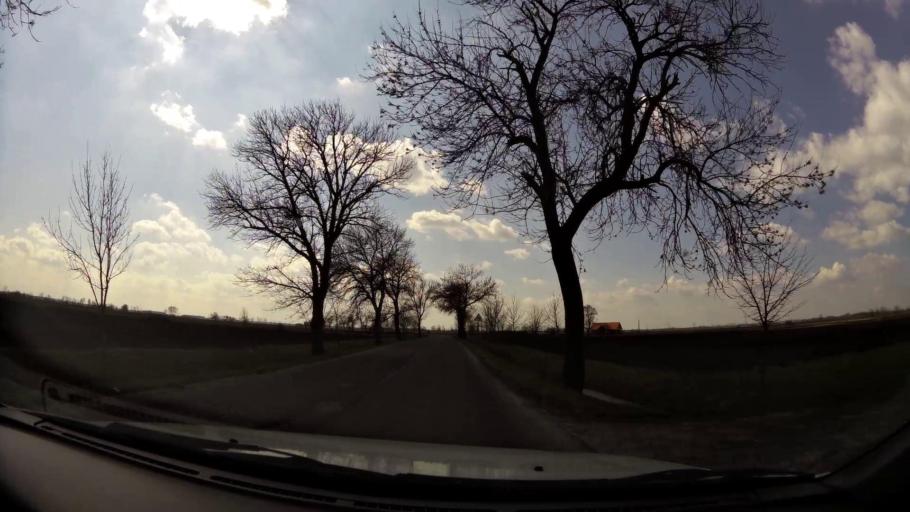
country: HU
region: Pest
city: Tapiogyorgye
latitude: 47.3384
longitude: 19.9324
